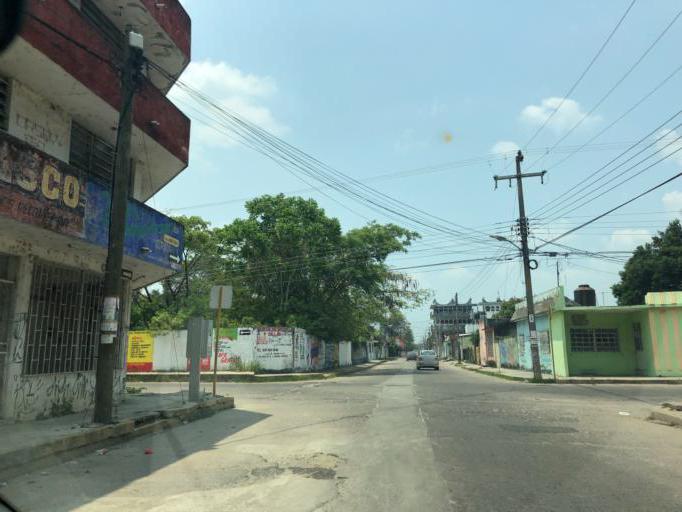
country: MX
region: Tabasco
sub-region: Cardenas
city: Cardenas
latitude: 17.9914
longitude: -93.3815
